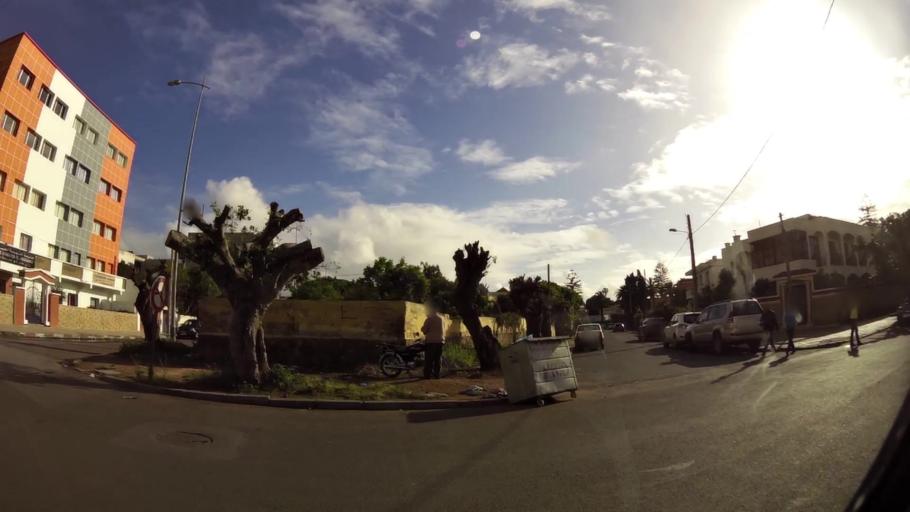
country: MA
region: Grand Casablanca
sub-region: Mohammedia
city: Mohammedia
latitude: 33.6978
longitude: -7.3908
